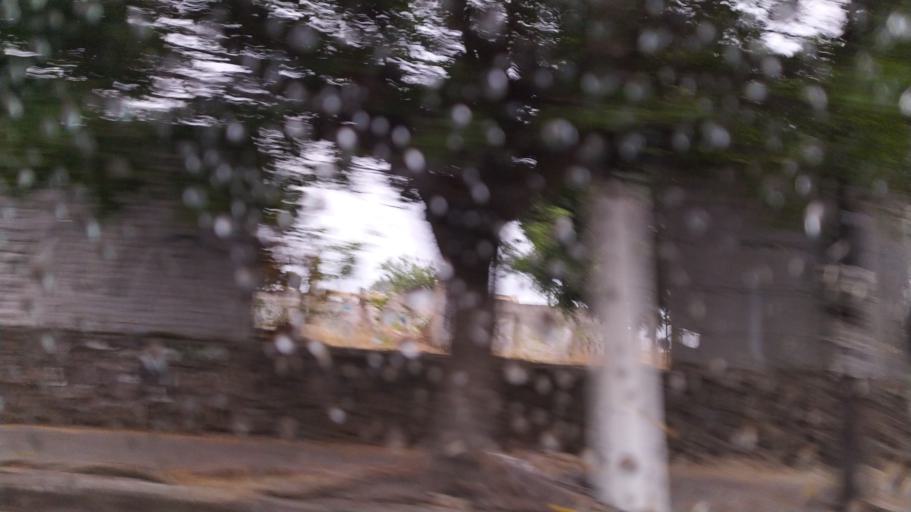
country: MX
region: Jalisco
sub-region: Zapopan
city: Zapopan
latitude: 20.7205
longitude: -103.3595
